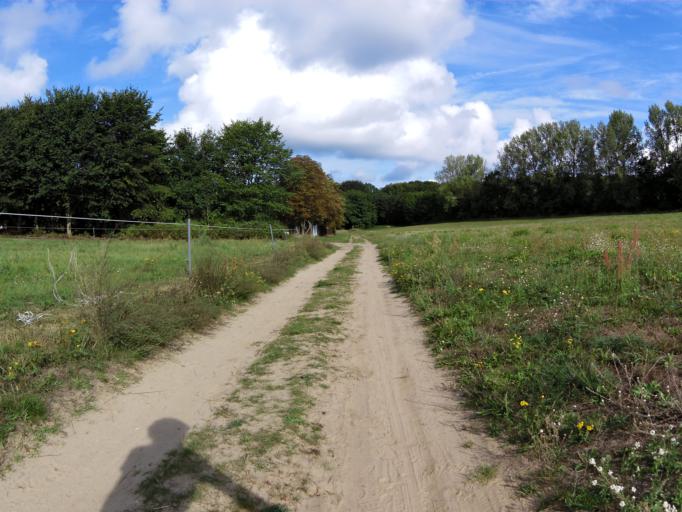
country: DE
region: Mecklenburg-Vorpommern
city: Seebad Bansin
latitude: 53.9657
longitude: 14.1231
